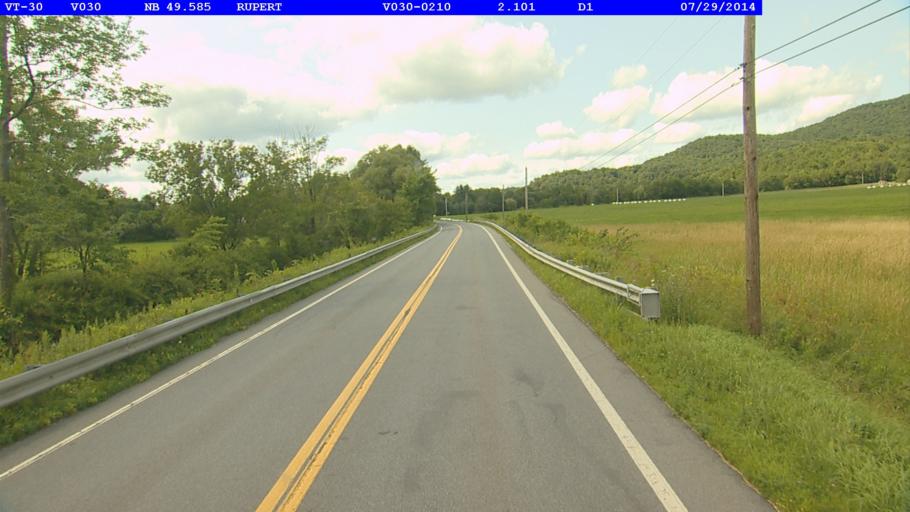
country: US
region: Vermont
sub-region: Bennington County
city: Manchester Center
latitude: 43.2962
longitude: -73.1431
